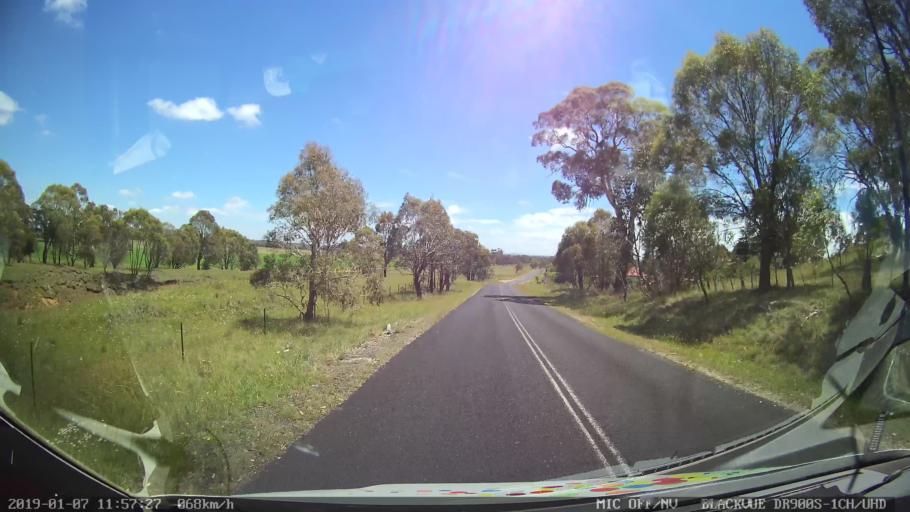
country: AU
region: New South Wales
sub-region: Guyra
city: Guyra
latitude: -30.2640
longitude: 151.6656
